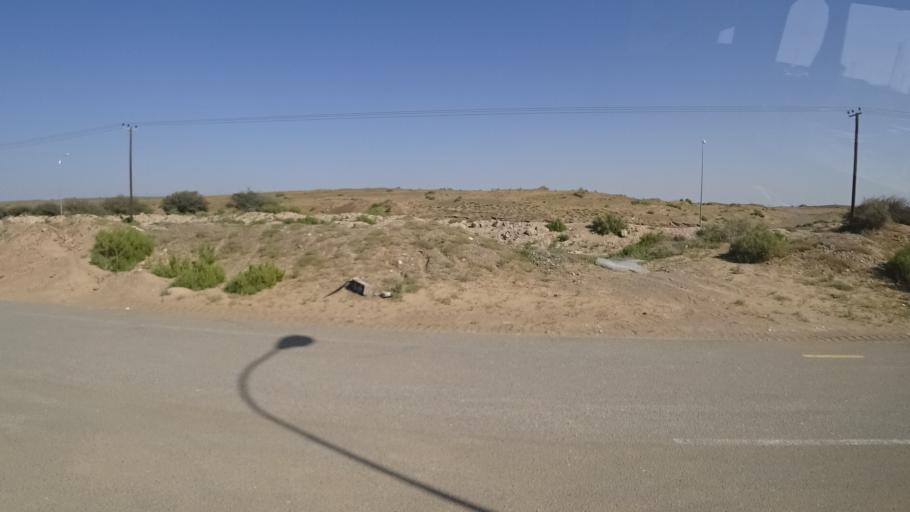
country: AE
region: Abu Dhabi
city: Al Ain
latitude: 23.9803
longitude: 55.8375
